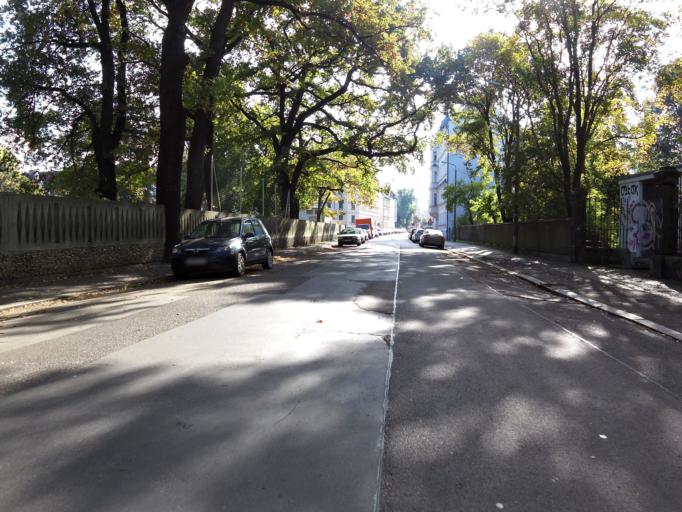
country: DE
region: Saxony
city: Leipzig
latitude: 51.3411
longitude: 12.3312
